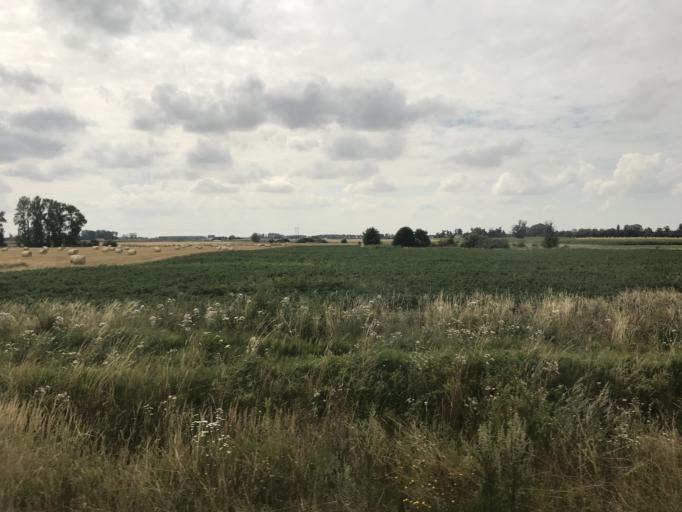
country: PL
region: Greater Poland Voivodeship
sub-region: Powiat gnieznienski
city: Niechanowo
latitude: 52.5338
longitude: 17.6748
